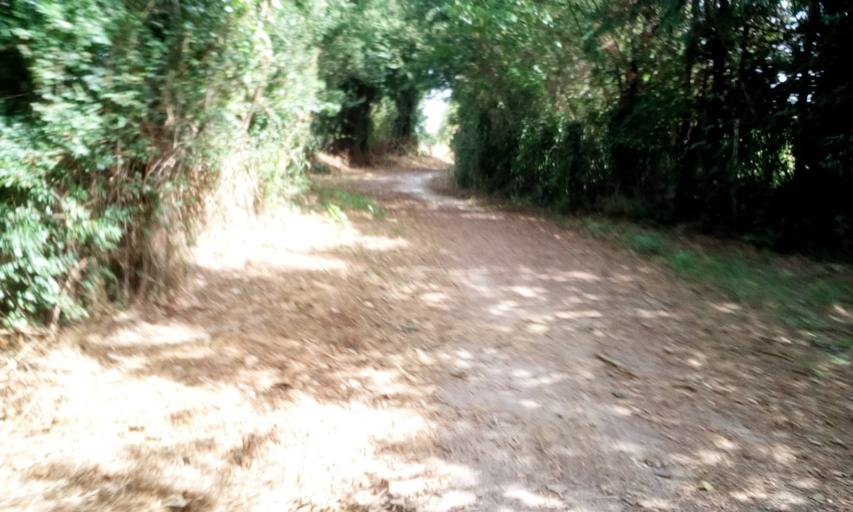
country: FR
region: Lower Normandy
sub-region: Departement du Calvados
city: Merville-Franceville-Plage
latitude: 49.2548
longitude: -0.1970
